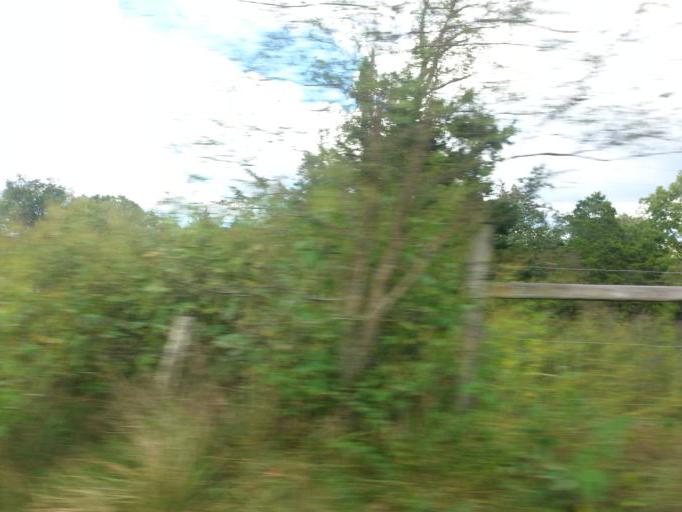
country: US
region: Tennessee
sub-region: Union County
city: Condon
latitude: 36.1262
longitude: -83.7768
